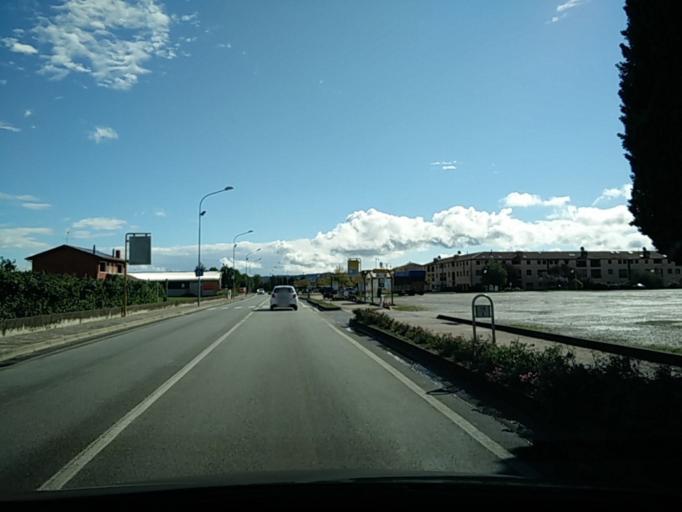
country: IT
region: Veneto
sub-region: Provincia di Treviso
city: Vidor
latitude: 45.8602
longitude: 12.0429
